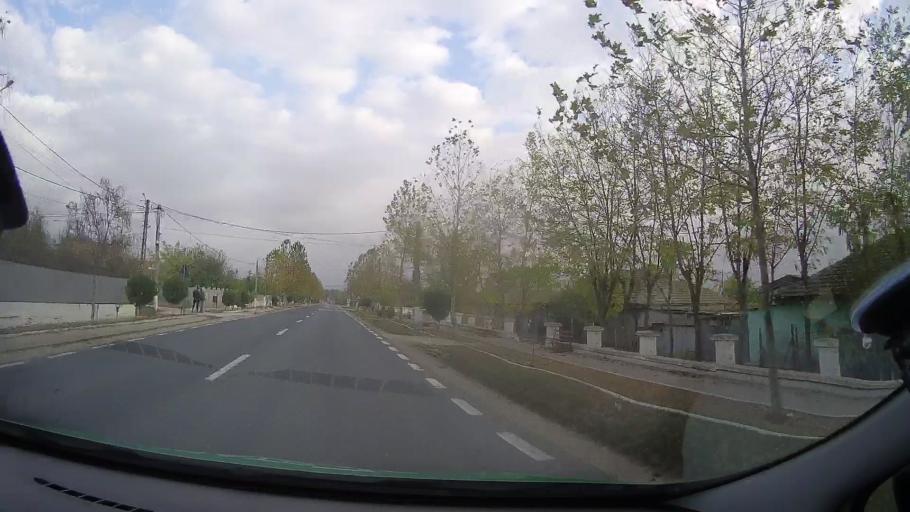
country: RO
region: Constanta
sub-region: Comuna Mircea Voda
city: Satu Nou
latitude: 44.2692
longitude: 28.2179
